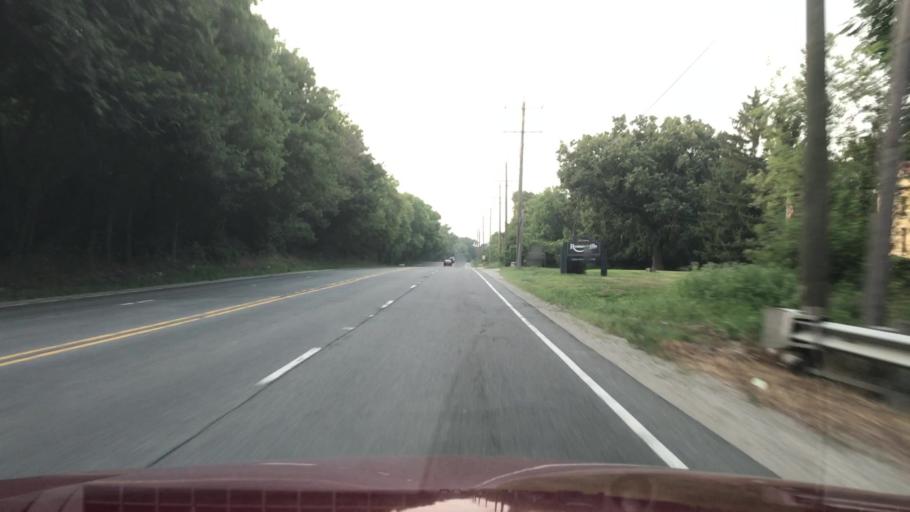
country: US
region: Illinois
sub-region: Will County
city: Lockport
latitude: 41.5997
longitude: -88.0750
